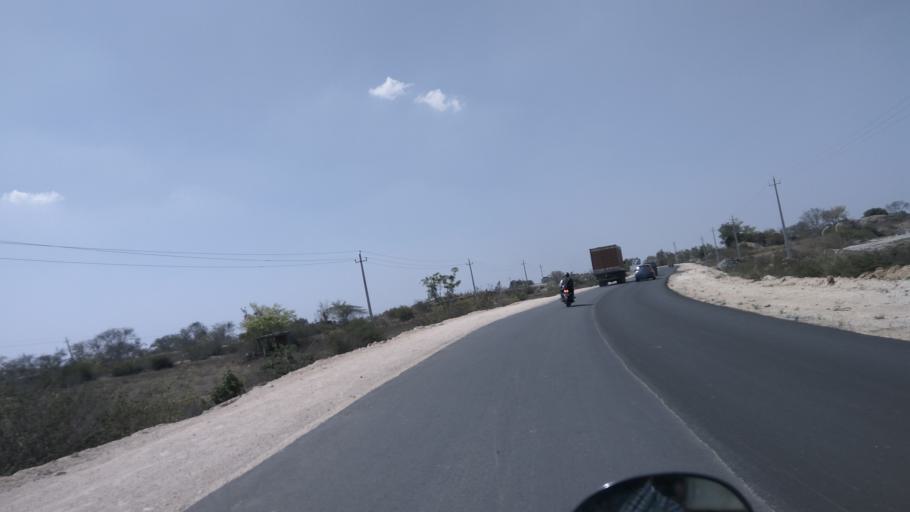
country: IN
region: Karnataka
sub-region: Kolar
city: Mulbagal
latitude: 13.1727
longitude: 78.3570
